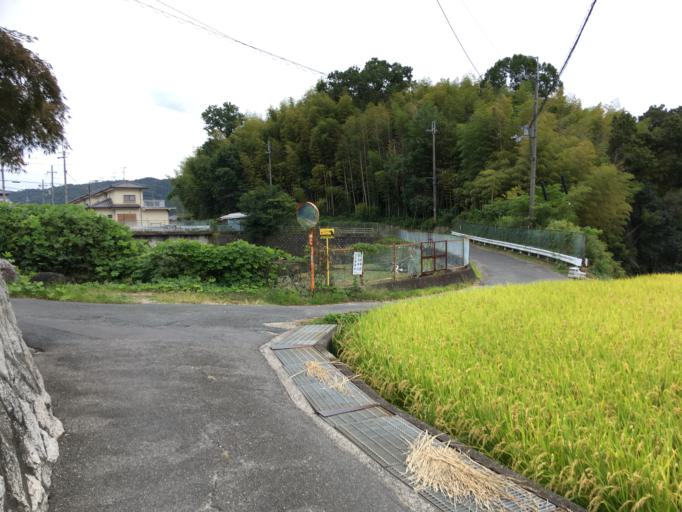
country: JP
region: Nara
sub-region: Ikoma-shi
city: Ikoma
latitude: 34.6201
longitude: 135.6964
